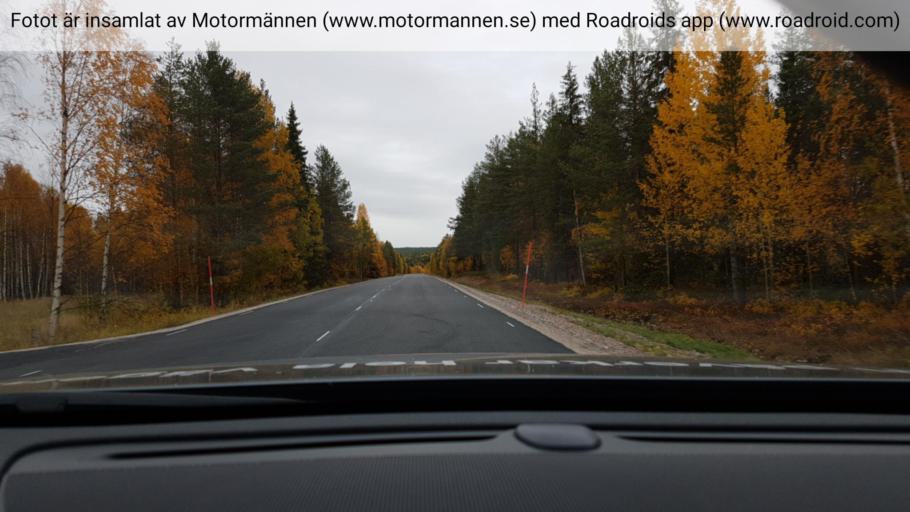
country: SE
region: Norrbotten
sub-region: Overkalix Kommun
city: OEverkalix
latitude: 66.4523
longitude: 22.7883
